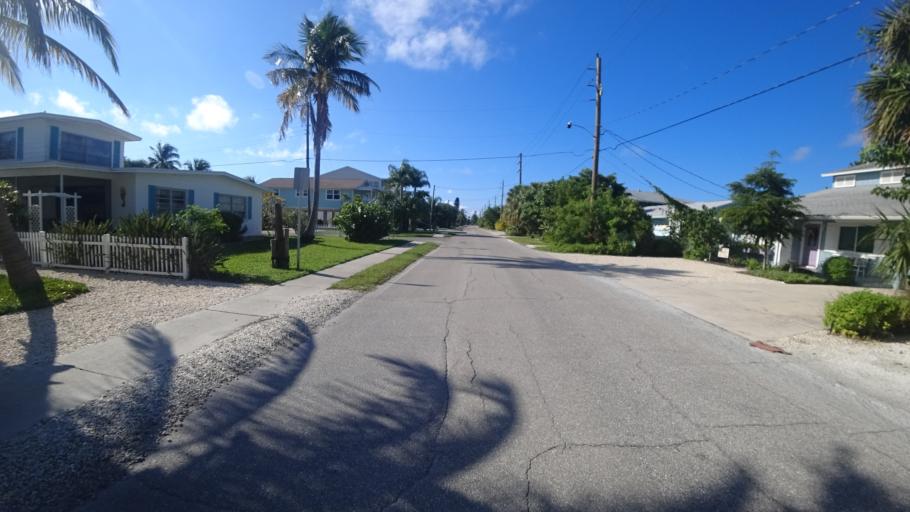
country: US
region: Florida
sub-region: Manatee County
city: Anna Maria
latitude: 27.5298
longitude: -82.7260
